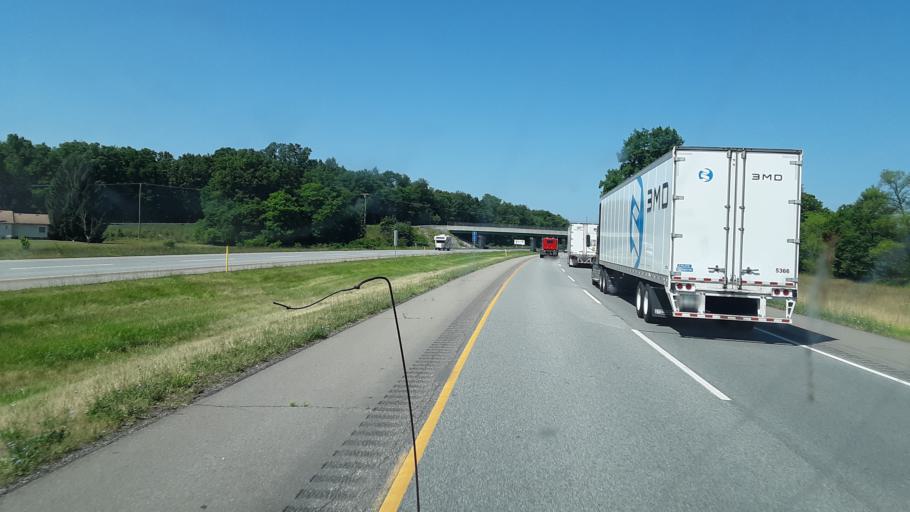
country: US
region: Indiana
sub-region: Saint Joseph County
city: Granger
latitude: 41.7323
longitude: -86.0478
